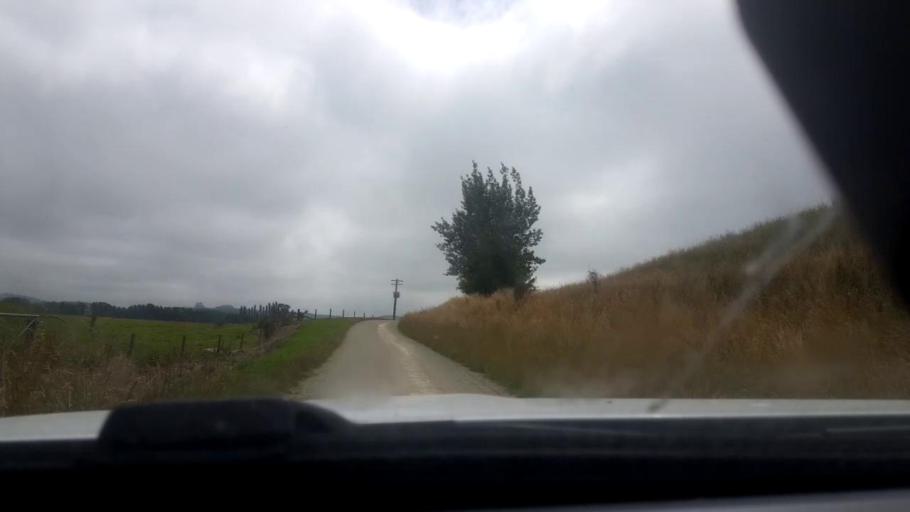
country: NZ
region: Canterbury
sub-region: Timaru District
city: Pleasant Point
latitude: -44.2130
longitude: 171.1086
